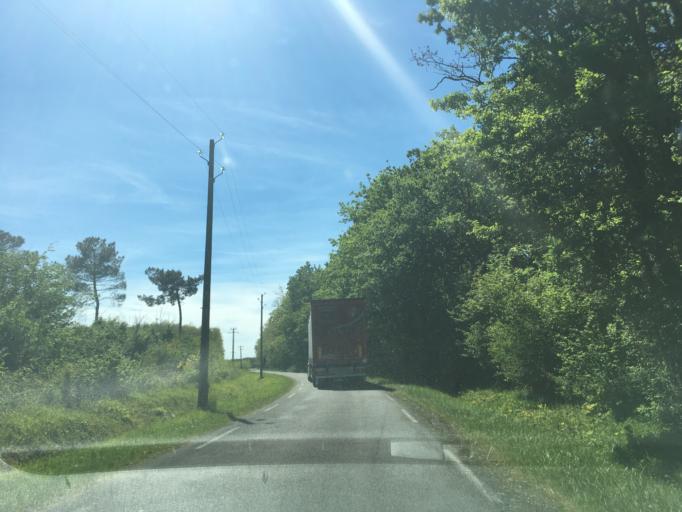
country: FR
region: Aquitaine
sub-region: Departement de la Gironde
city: Lesparre-Medoc
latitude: 45.2652
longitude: -0.9007
